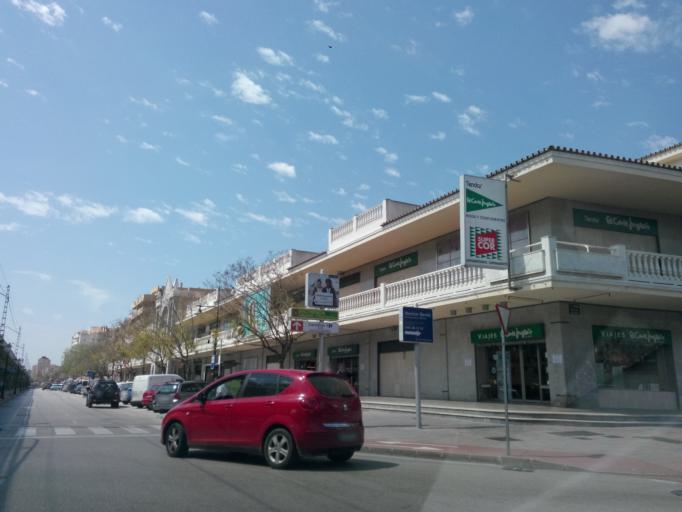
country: ES
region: Andalusia
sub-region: Provincia de Malaga
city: Fuengirola
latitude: 36.5551
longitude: -4.6143
